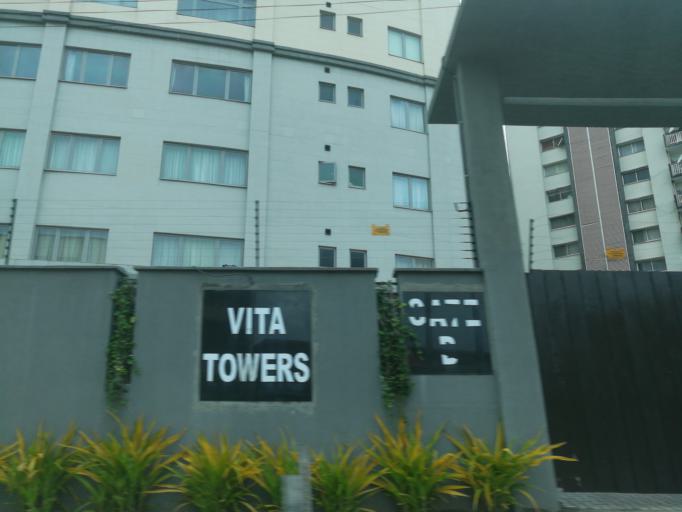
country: NG
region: Lagos
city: Lagos
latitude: 6.4355
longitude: 3.4146
